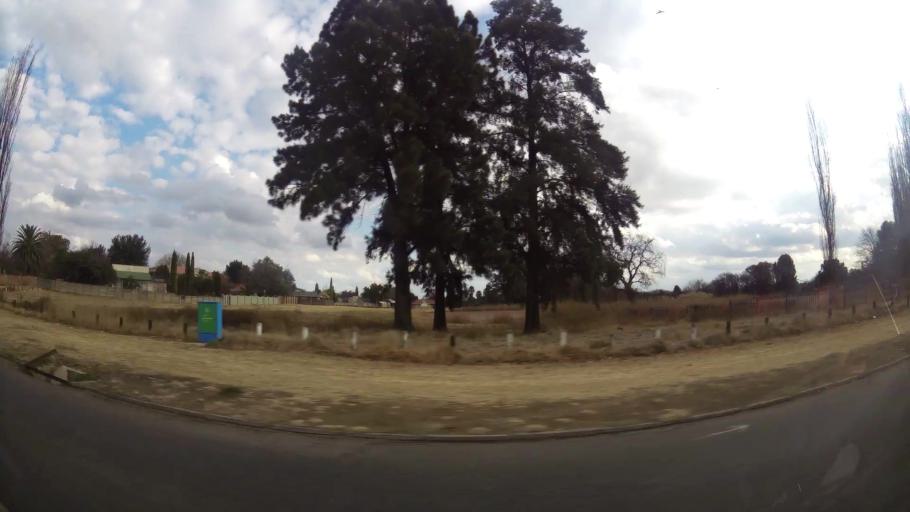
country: ZA
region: Orange Free State
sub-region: Fezile Dabi District Municipality
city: Sasolburg
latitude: -26.8034
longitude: 27.8122
